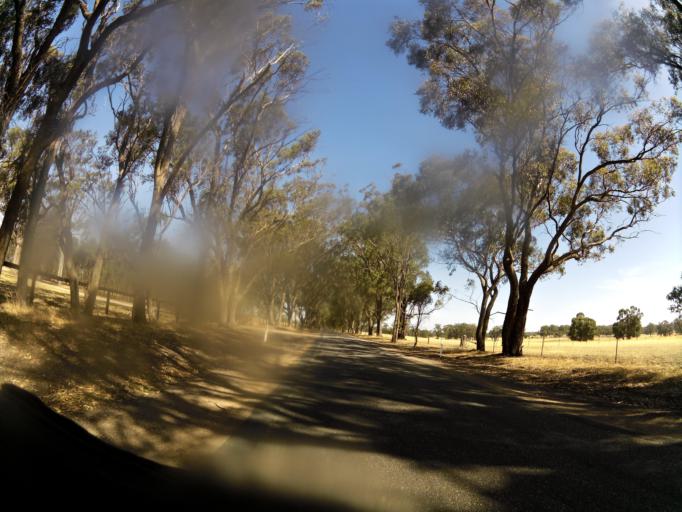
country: AU
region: Victoria
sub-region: Campaspe
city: Kyabram
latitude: -36.8877
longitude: 145.1014
